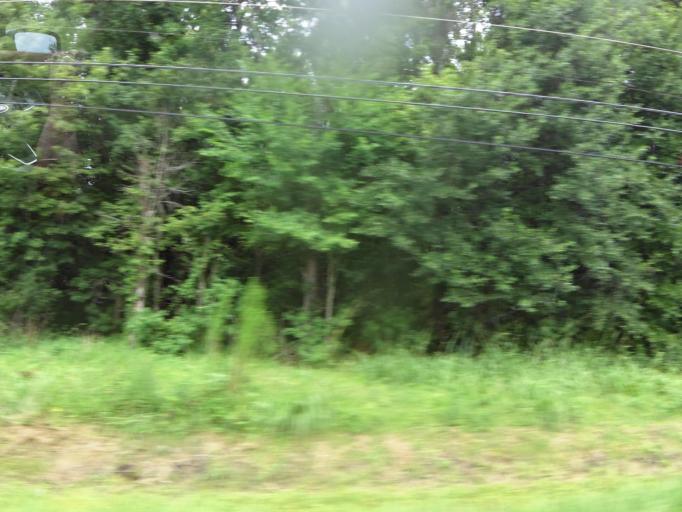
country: US
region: Florida
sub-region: Nassau County
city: Nassau Village-Ratliff
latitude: 30.4468
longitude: -81.7755
